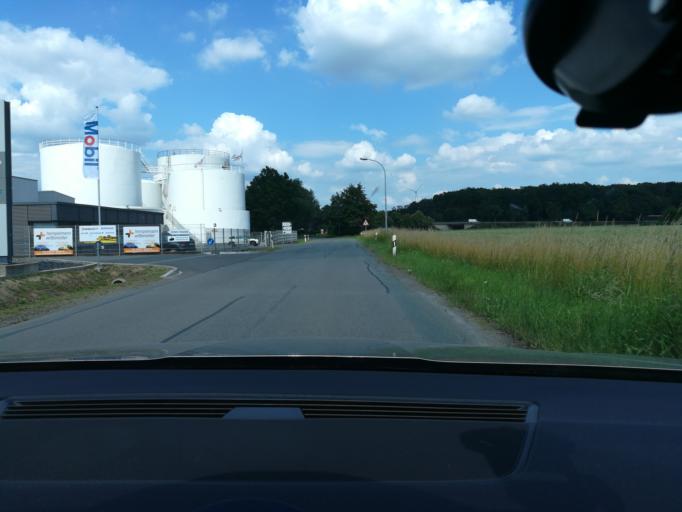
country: DE
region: North Rhine-Westphalia
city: Lubbecke
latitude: 52.3316
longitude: 8.6160
